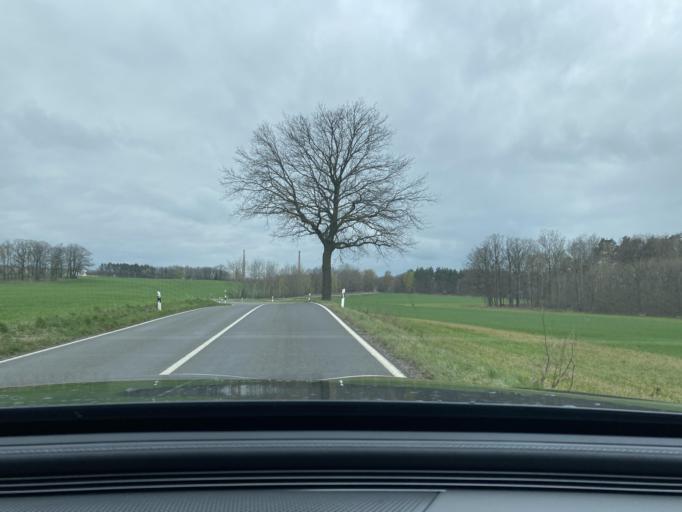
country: DE
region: Saxony
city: Puschwitz
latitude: 51.2623
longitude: 14.3121
